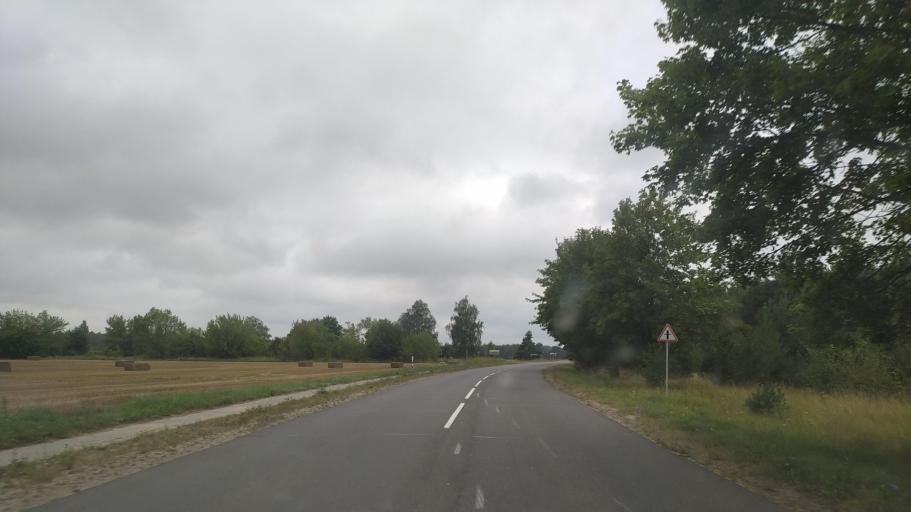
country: BY
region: Brest
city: Byaroza
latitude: 52.5565
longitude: 24.9172
